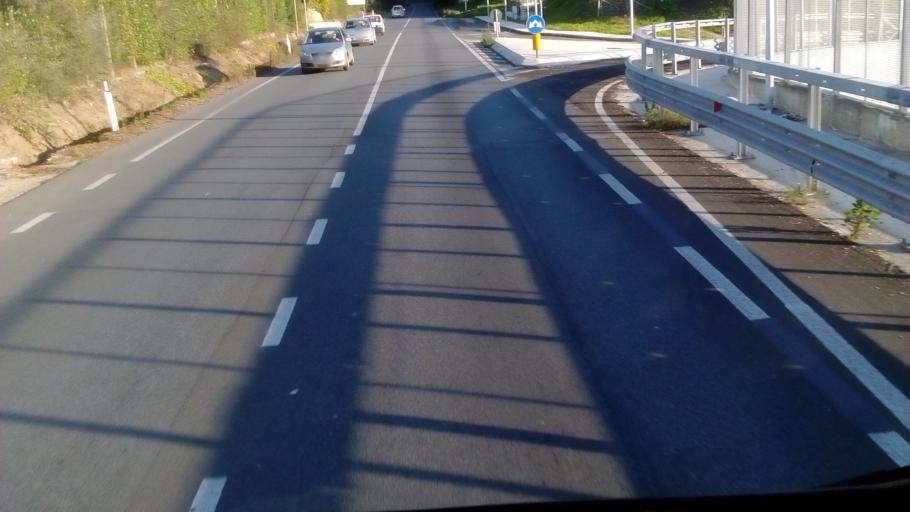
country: IT
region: Latium
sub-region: Citta metropolitana di Roma Capitale
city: Albano Laziale
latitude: 41.7175
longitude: 12.6255
